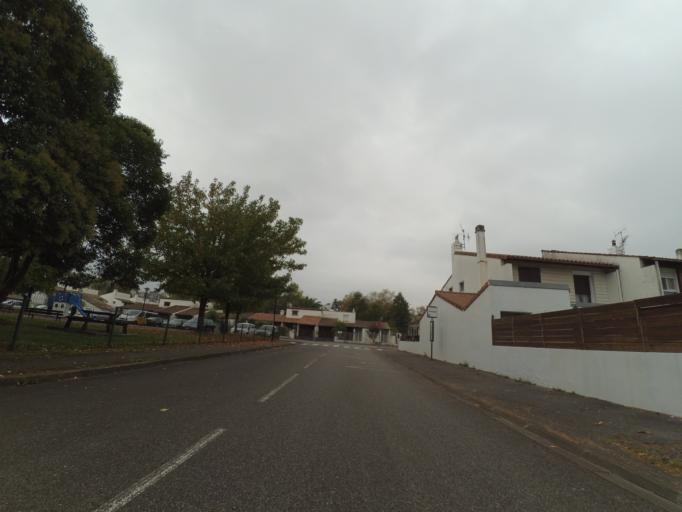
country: ES
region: Basque Country
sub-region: Provincia de Guipuzcoa
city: Irun
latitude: 43.3448
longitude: -1.7693
